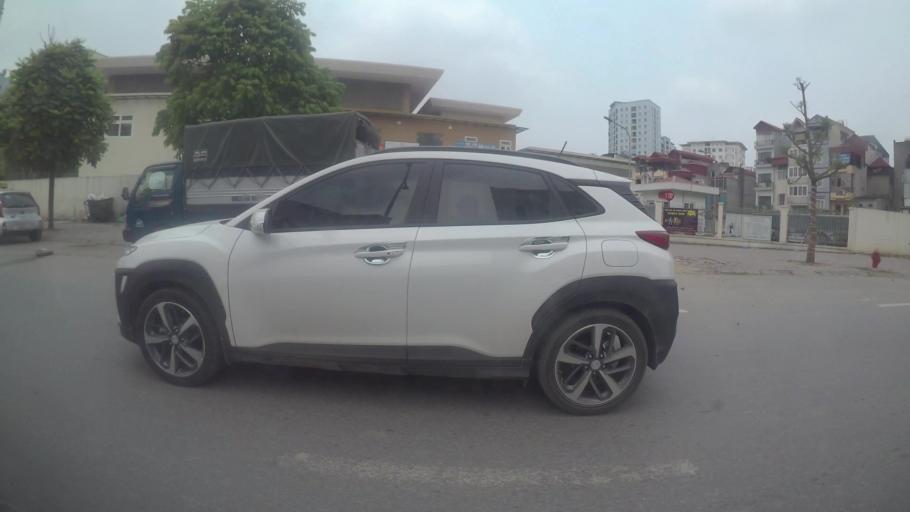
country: VN
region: Ha Noi
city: Cau Dien
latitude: 21.0324
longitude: 105.7736
